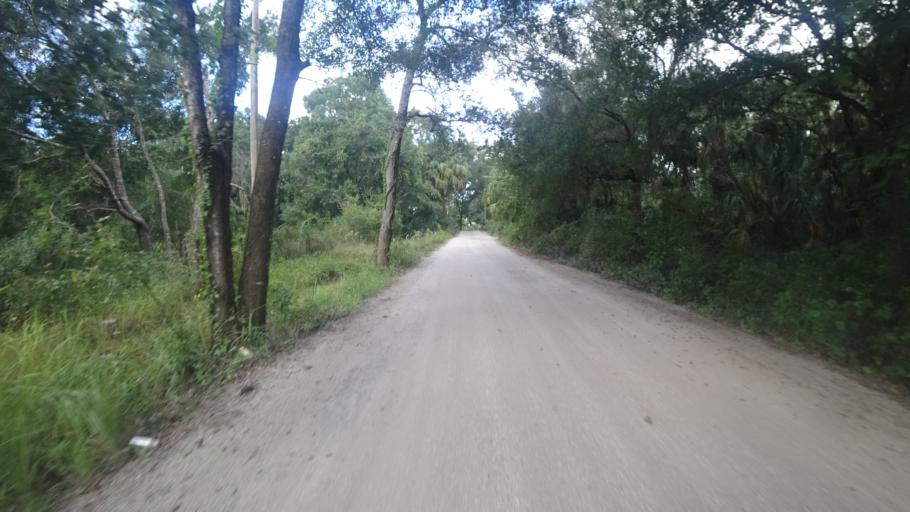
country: US
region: Florida
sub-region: Hillsborough County
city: Sun City Center
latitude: 27.6473
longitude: -82.3756
